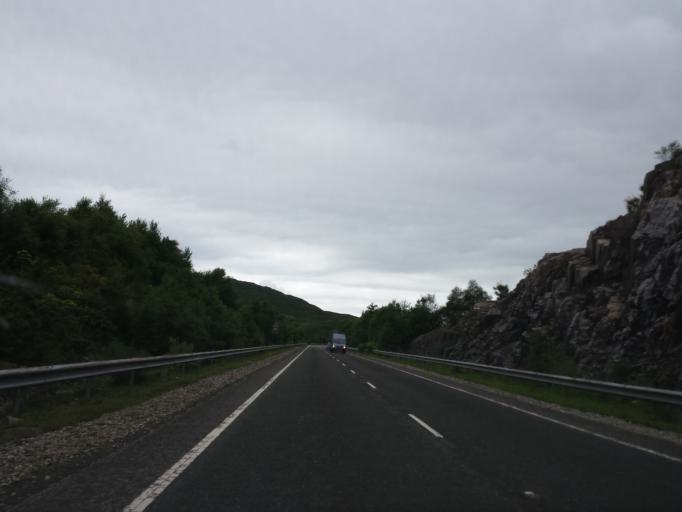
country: GB
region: Scotland
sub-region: Argyll and Bute
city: Isle Of Mull
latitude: 56.8804
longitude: -5.6850
